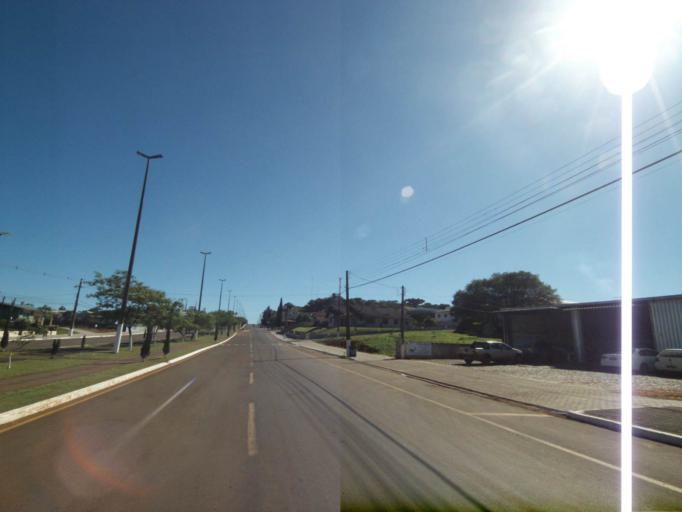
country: BR
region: Parana
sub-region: Pato Branco
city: Pato Branco
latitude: -26.2636
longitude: -52.7789
